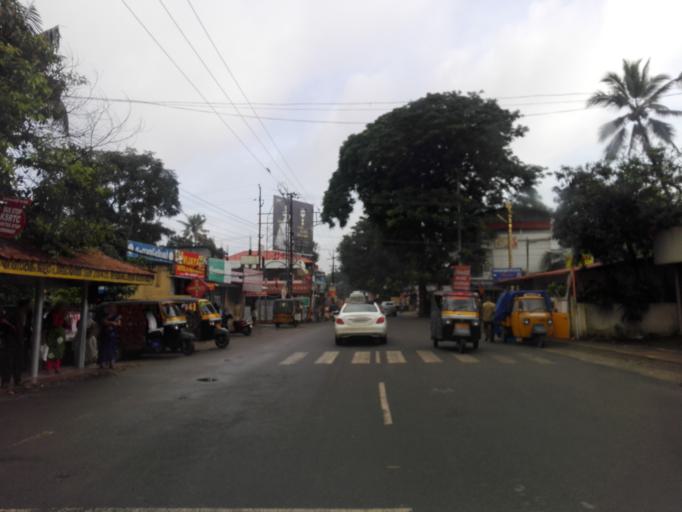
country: IN
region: Kerala
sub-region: Alappuzha
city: Arukutti
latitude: 9.9137
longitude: 76.3637
